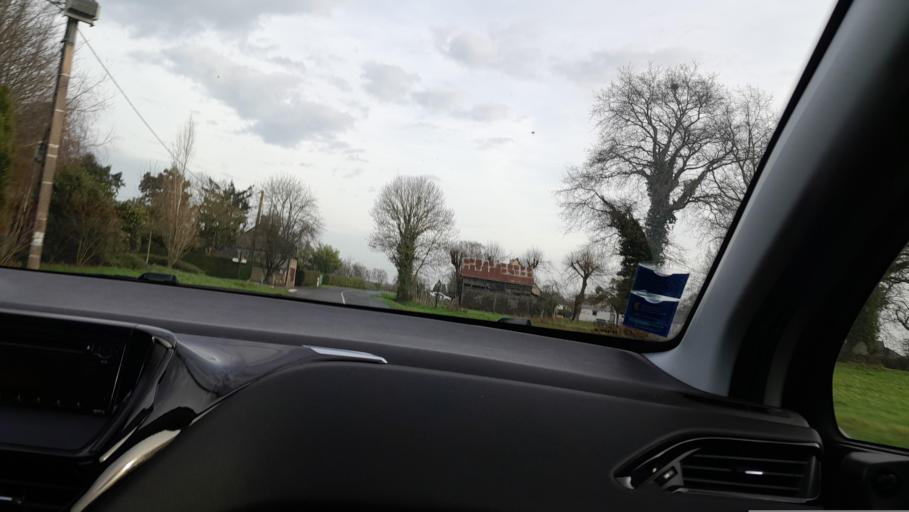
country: FR
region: Brittany
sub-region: Departement d'Ille-et-Vilaine
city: La Guerche-de-Bretagne
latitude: 47.9485
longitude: -1.2010
